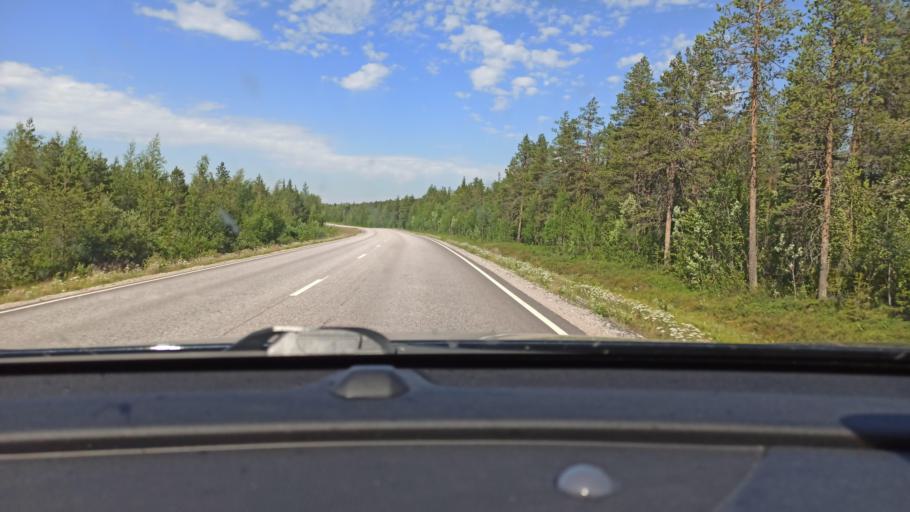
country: FI
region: Lapland
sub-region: Tunturi-Lappi
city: Muonio
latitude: 67.9893
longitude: 23.6391
